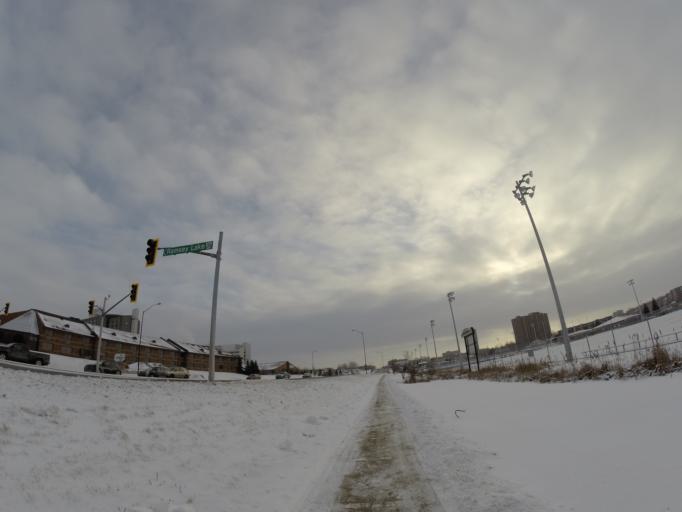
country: CA
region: Ontario
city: Greater Sudbury
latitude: 46.4699
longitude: -80.9982
